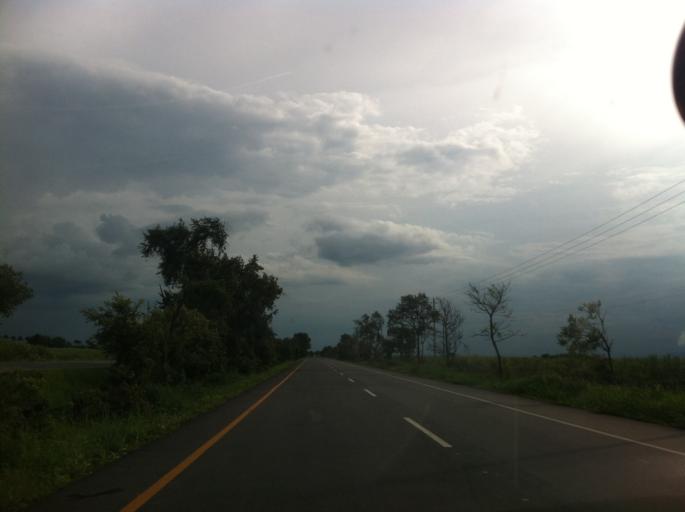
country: CO
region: Valle del Cauca
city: Palmira
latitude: 3.5557
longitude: -76.3365
